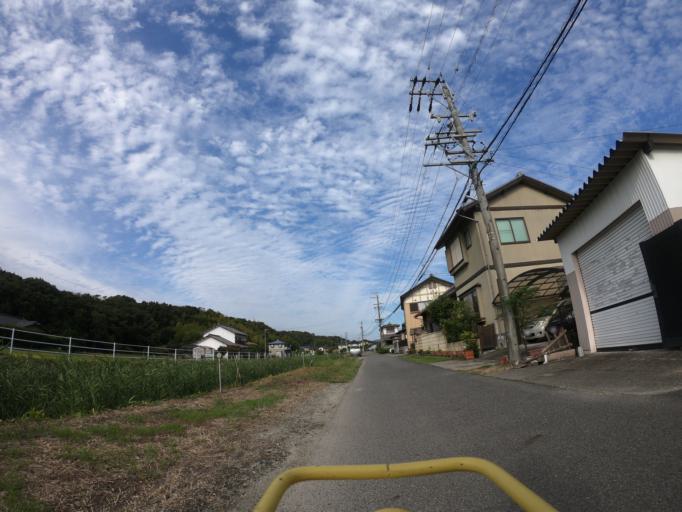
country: JP
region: Aichi
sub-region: Toyota-shi
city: Toyota
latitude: 35.1390
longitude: 137.0770
